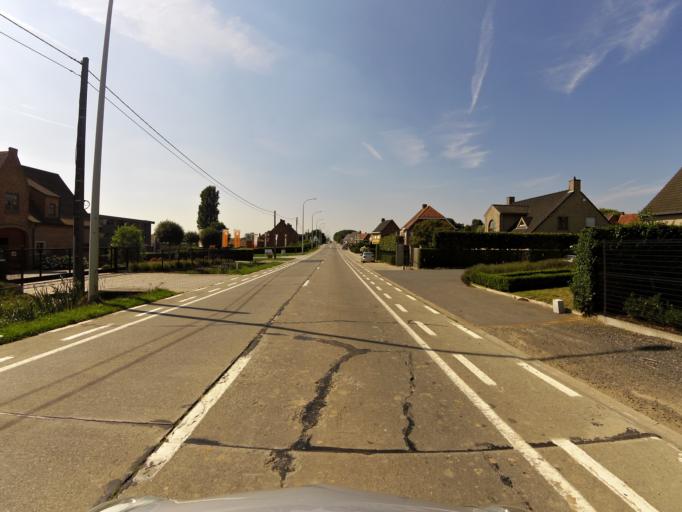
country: BE
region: Flanders
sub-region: Provincie West-Vlaanderen
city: Dentergem
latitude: 50.9921
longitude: 3.4161
